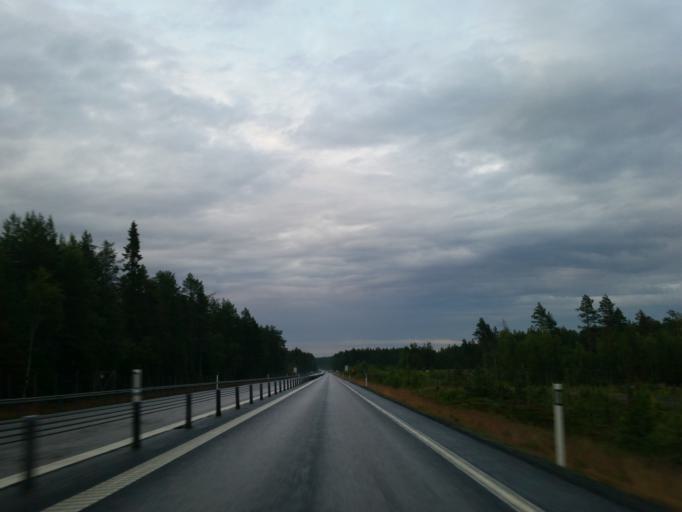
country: SE
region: Vaesterbotten
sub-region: Robertsfors Kommun
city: Robertsfors
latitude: 63.9911
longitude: 20.7562
